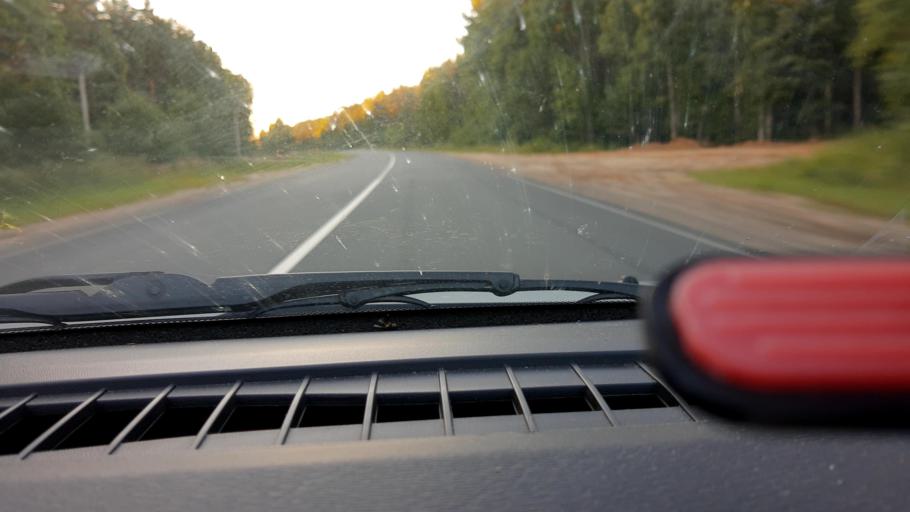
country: RU
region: Nizjnij Novgorod
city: Uren'
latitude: 57.3734
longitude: 45.6929
